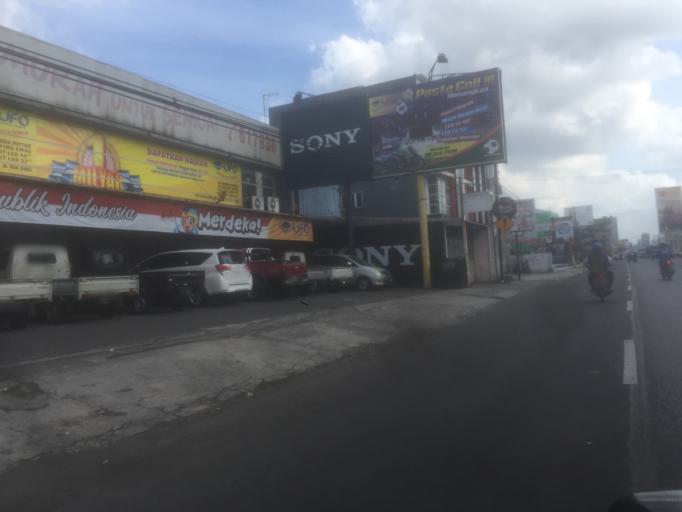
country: ID
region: Daerah Istimewa Yogyakarta
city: Yogyakarta
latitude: -7.7681
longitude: 110.3615
